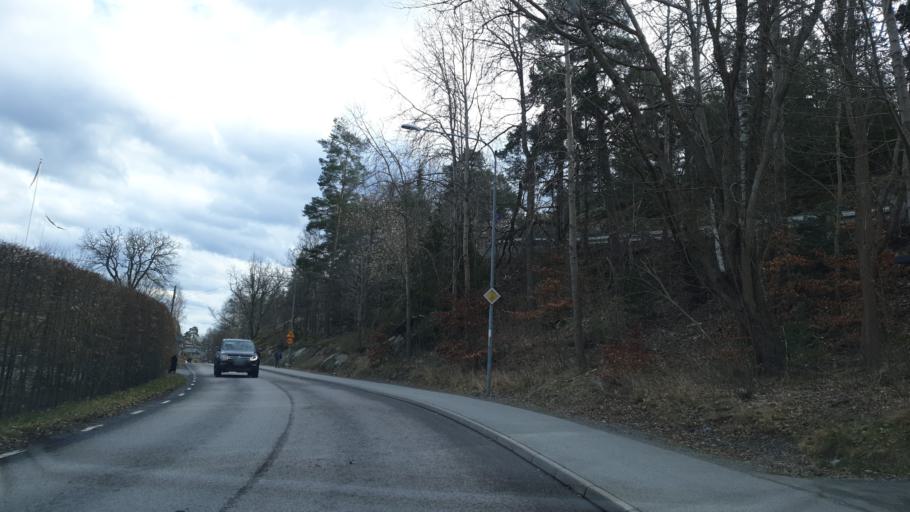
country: SE
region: Stockholm
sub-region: Nacka Kommun
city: Saltsjobaden
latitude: 59.2729
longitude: 18.3059
